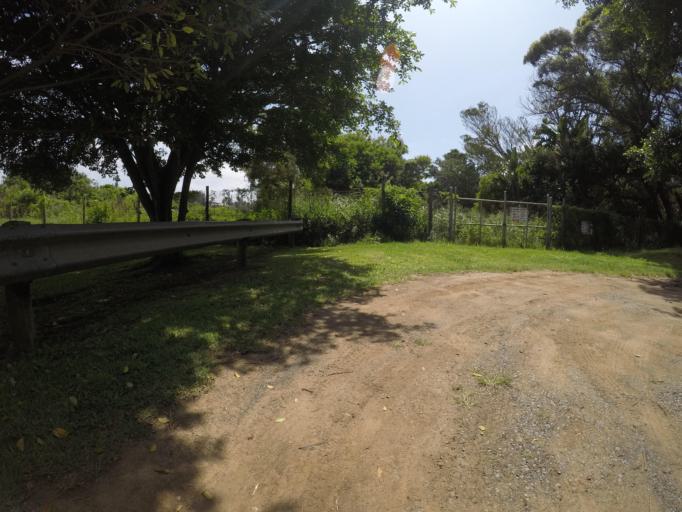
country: ZA
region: Eastern Cape
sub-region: Buffalo City Metropolitan Municipality
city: East London
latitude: -32.9455
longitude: 28.0214
